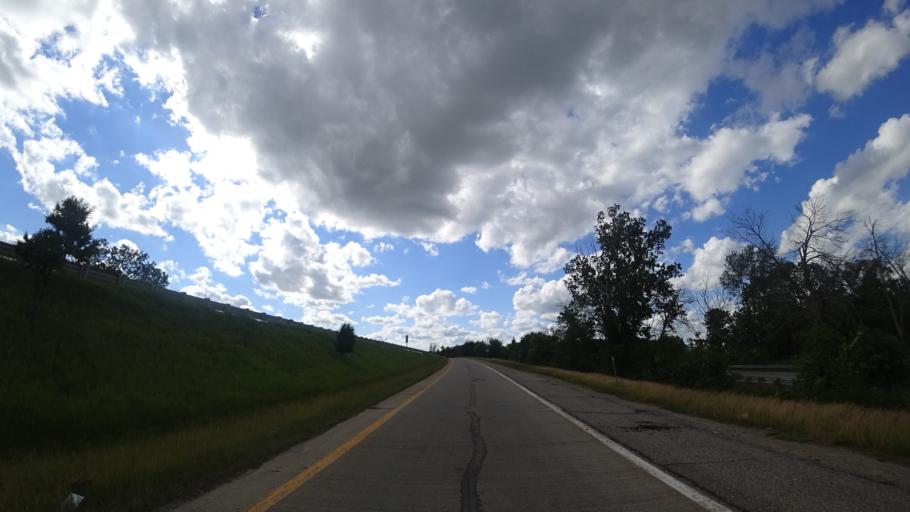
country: US
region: Michigan
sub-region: Ionia County
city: Portland
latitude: 42.8739
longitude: -84.9648
